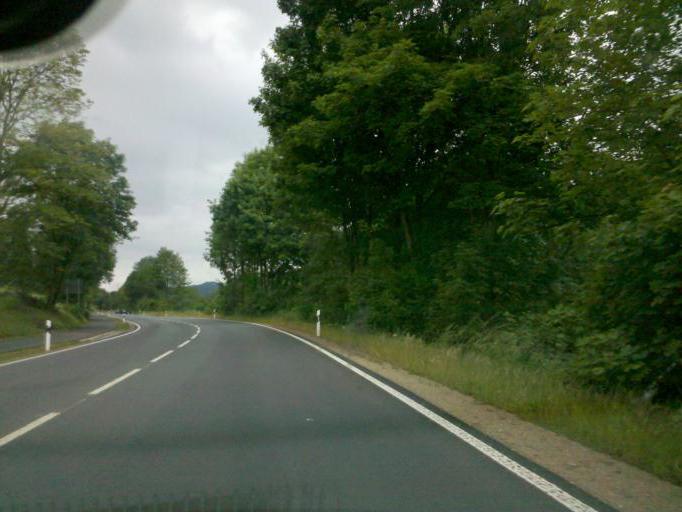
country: DE
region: North Rhine-Westphalia
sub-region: Regierungsbezirk Arnsberg
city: Lennestadt
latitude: 51.1679
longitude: 8.1068
